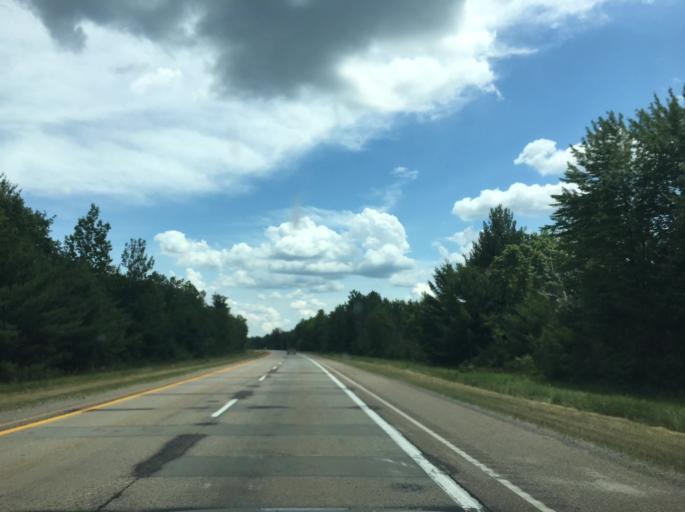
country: US
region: Michigan
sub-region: Ogemaw County
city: West Branch
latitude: 44.1719
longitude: -84.1706
